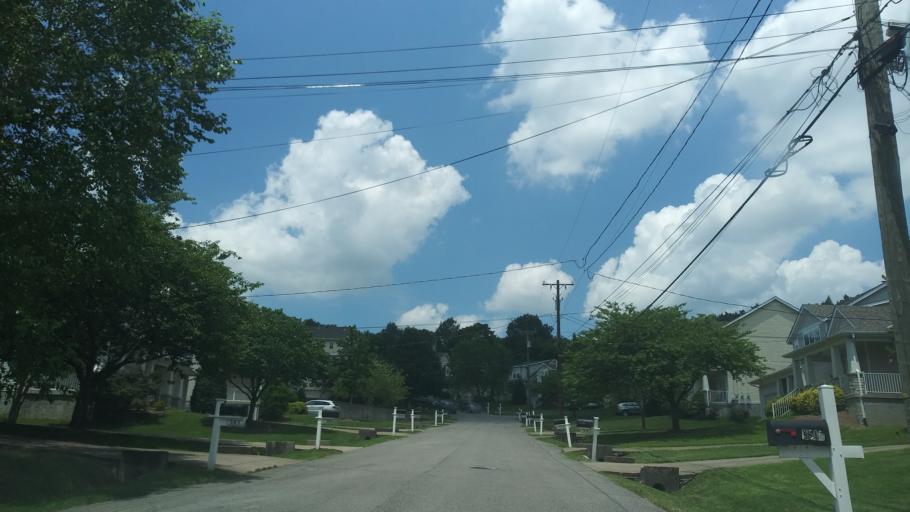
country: US
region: Tennessee
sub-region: Davidson County
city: Nashville
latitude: 36.1466
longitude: -86.8255
